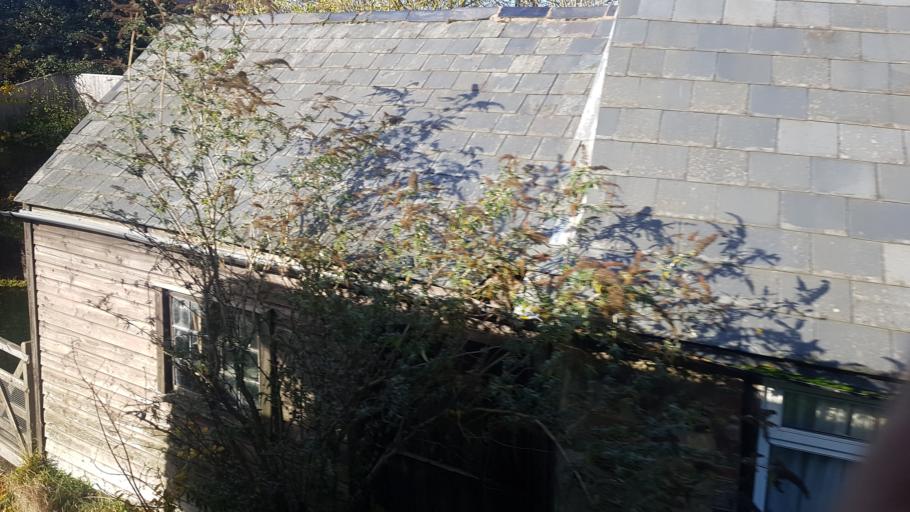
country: GB
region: England
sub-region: Isle of Wight
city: Shalfleet
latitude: 50.6425
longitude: -1.3927
